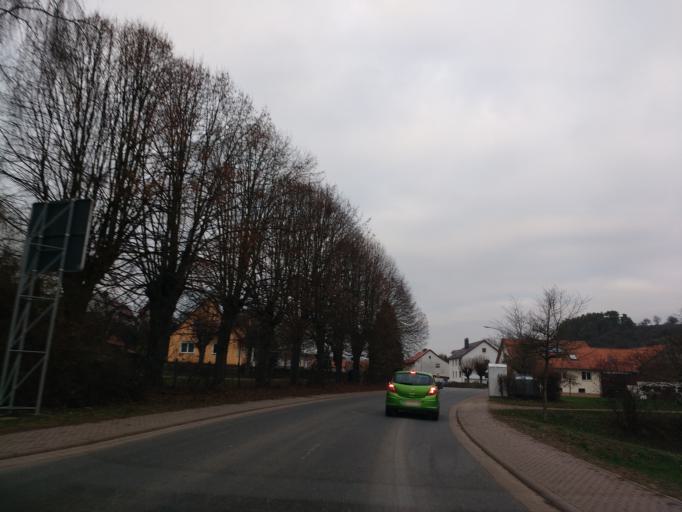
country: DE
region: Hesse
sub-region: Regierungsbezirk Kassel
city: Rotenburg an der Fulda
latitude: 51.0317
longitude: 9.7681
